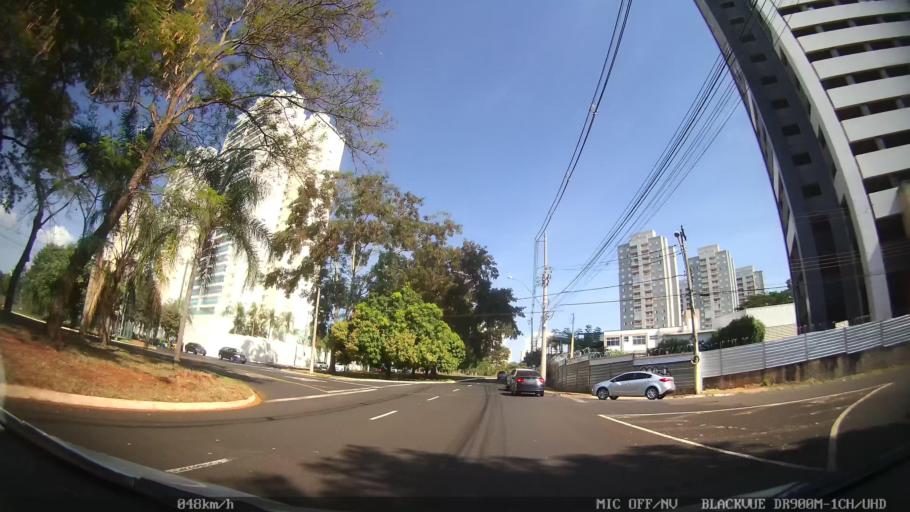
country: BR
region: Sao Paulo
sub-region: Ribeirao Preto
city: Ribeirao Preto
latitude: -21.2132
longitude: -47.8201
